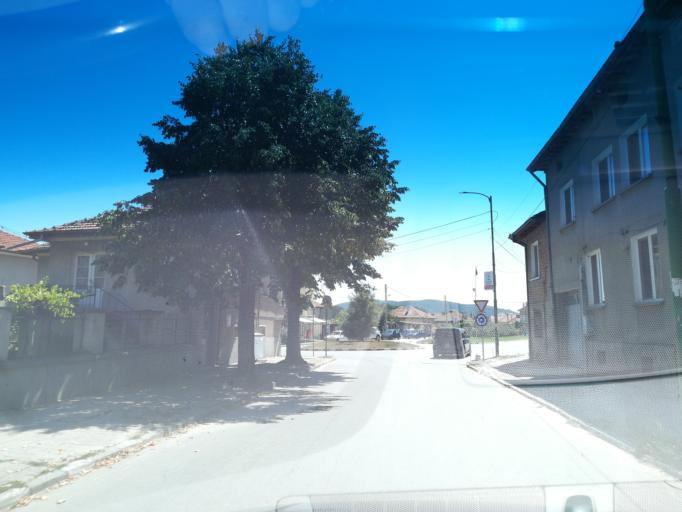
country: BG
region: Pazardzhik
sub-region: Obshtina Strelcha
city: Strelcha
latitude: 42.5040
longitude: 24.3216
